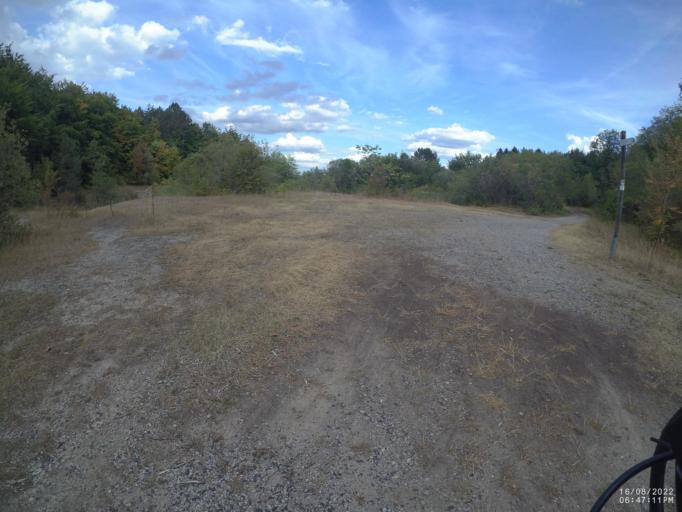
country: DE
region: Rheinland-Pfalz
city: Berndorf
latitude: 50.3150
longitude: 6.7144
